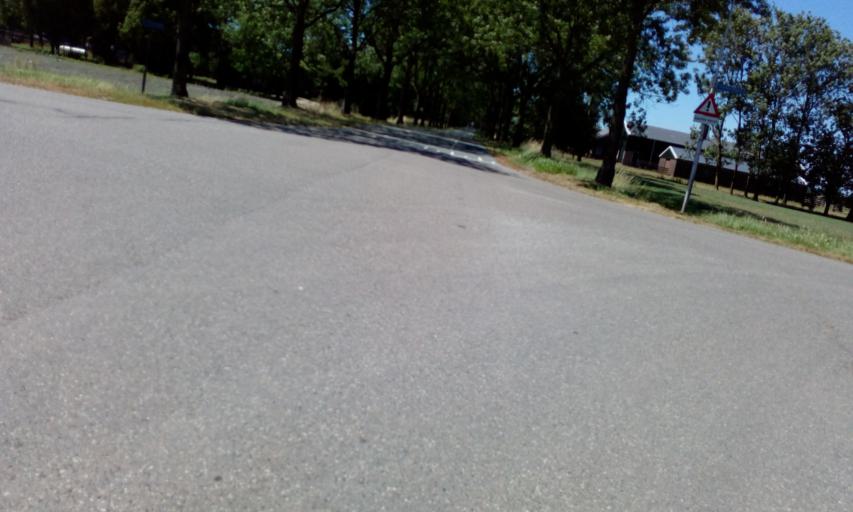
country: NL
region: South Holland
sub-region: Gemeente Alphen aan den Rijn
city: Alphen aan den Rijn
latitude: 52.1037
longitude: 4.6874
